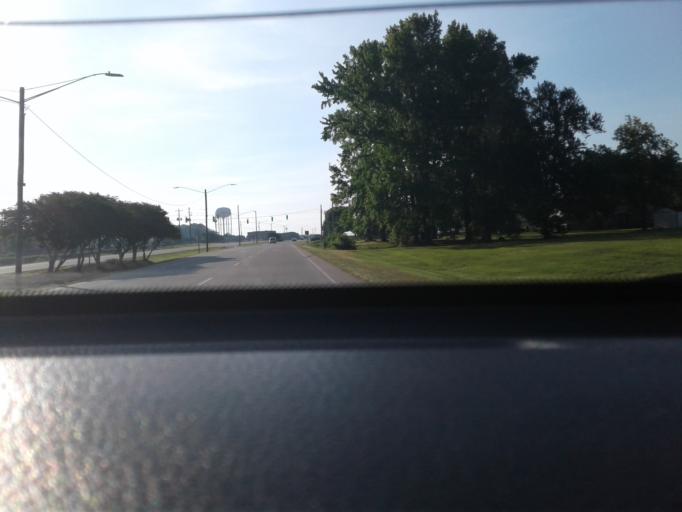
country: US
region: North Carolina
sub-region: Harnett County
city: Dunn
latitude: 35.3212
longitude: -78.6373
